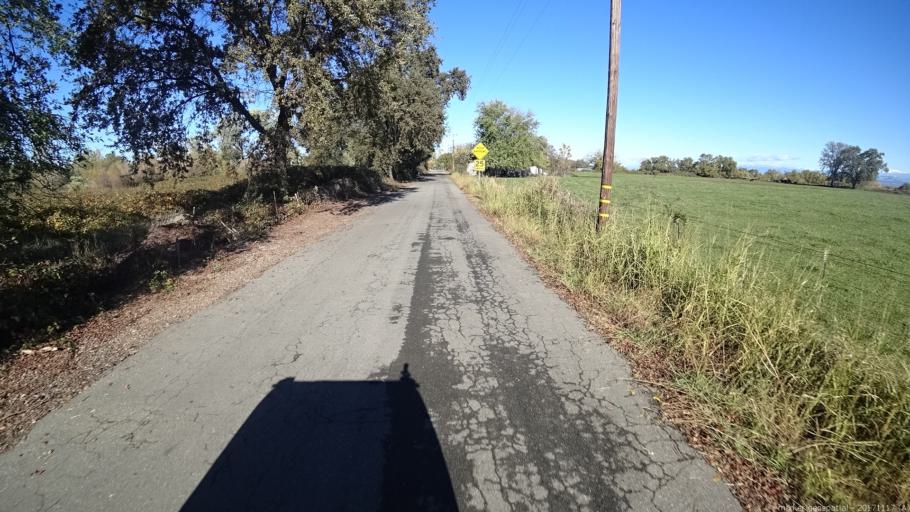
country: US
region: California
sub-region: Shasta County
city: Anderson
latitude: 40.4270
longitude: -122.2594
